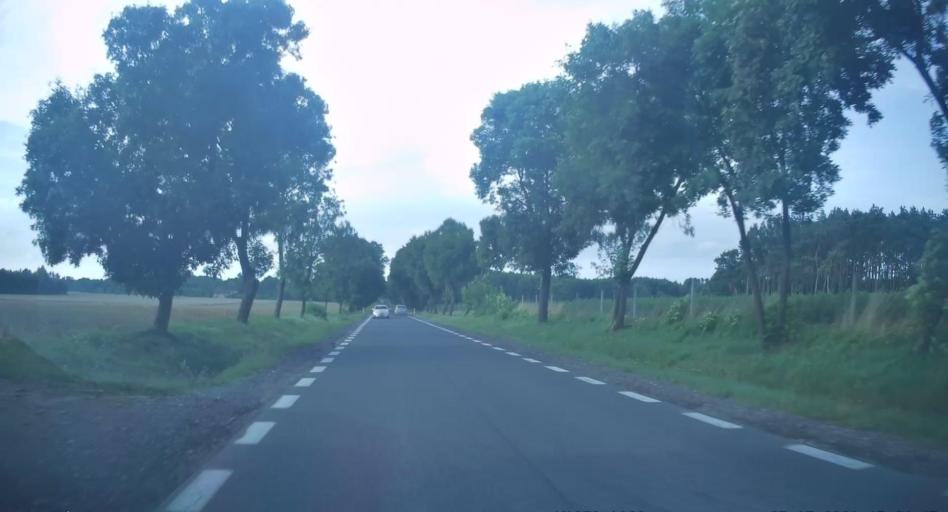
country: PL
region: Lodz Voivodeship
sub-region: Powiat tomaszowski
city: Rzeczyca
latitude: 51.6372
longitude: 20.2889
